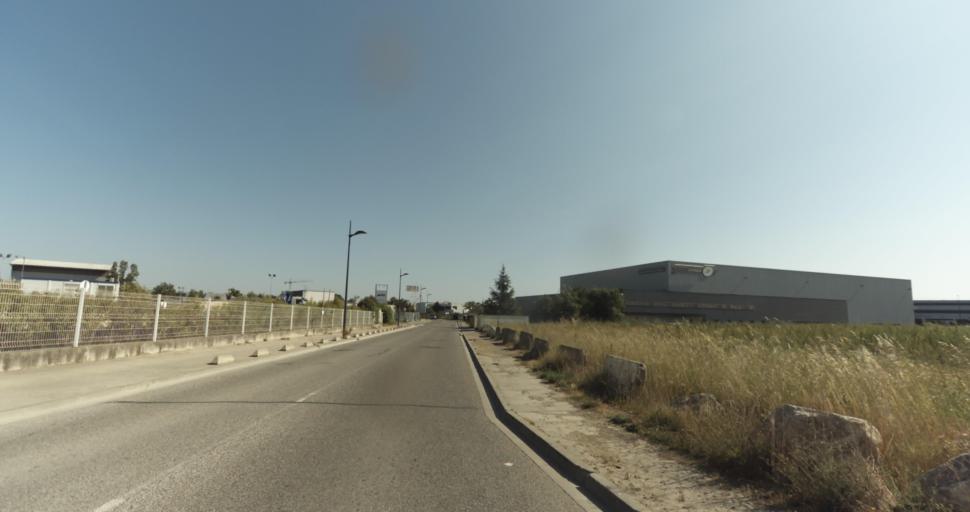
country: FR
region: Midi-Pyrenees
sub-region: Departement de la Haute-Garonne
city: Tournefeuille
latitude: 43.5926
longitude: 1.2999
